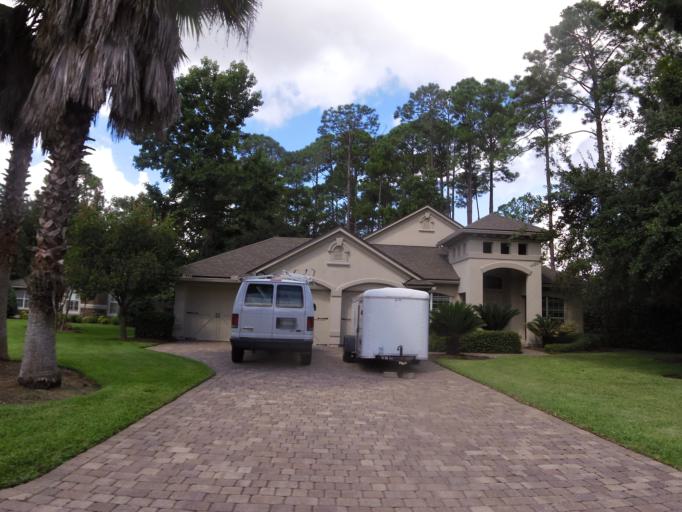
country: US
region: Florida
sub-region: Nassau County
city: Fernandina Beach
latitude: 30.6252
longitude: -81.4600
